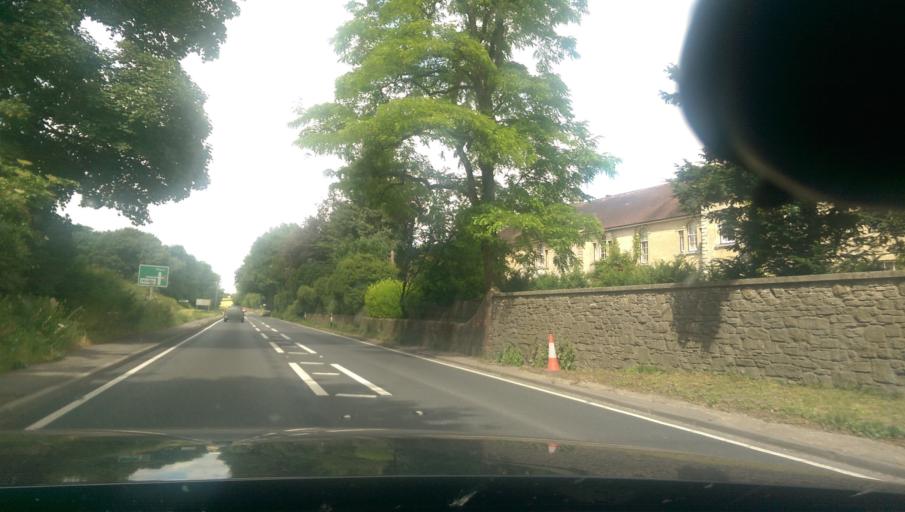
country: GB
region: England
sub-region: Wiltshire
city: Chicklade
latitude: 51.1095
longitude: -2.1274
